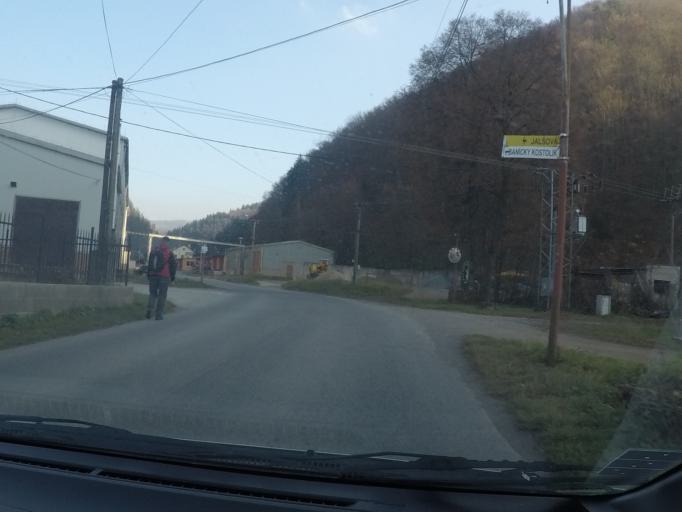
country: SK
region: Banskobystricky
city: Zarnovica
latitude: 48.4536
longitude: 18.7793
